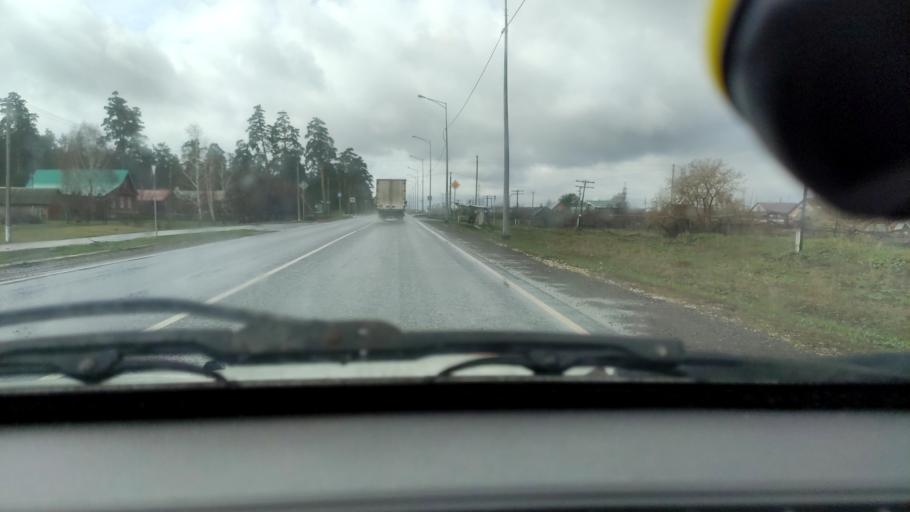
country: RU
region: Samara
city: Povolzhskiy
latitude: 53.5833
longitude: 49.5685
